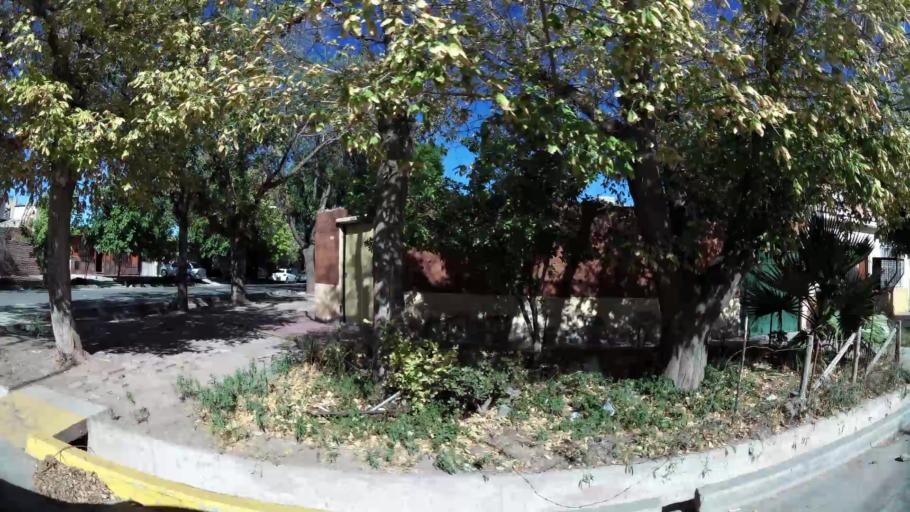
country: AR
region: Mendoza
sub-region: Departamento de Godoy Cruz
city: Godoy Cruz
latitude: -32.9303
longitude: -68.8622
